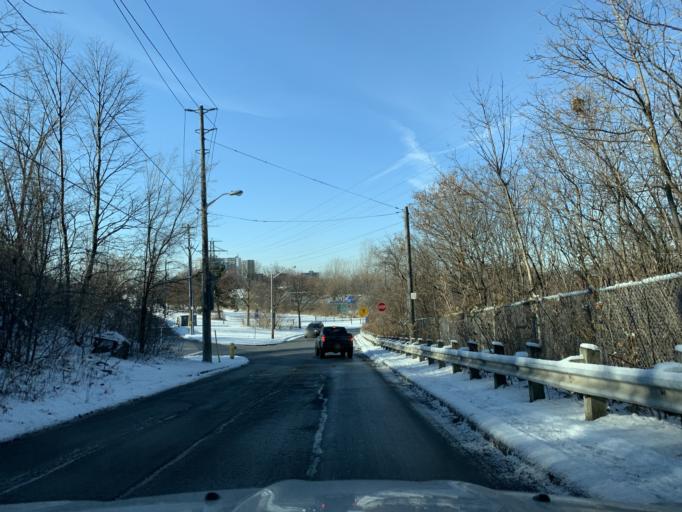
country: CA
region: Ontario
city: Toronto
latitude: 43.6739
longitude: -79.4804
